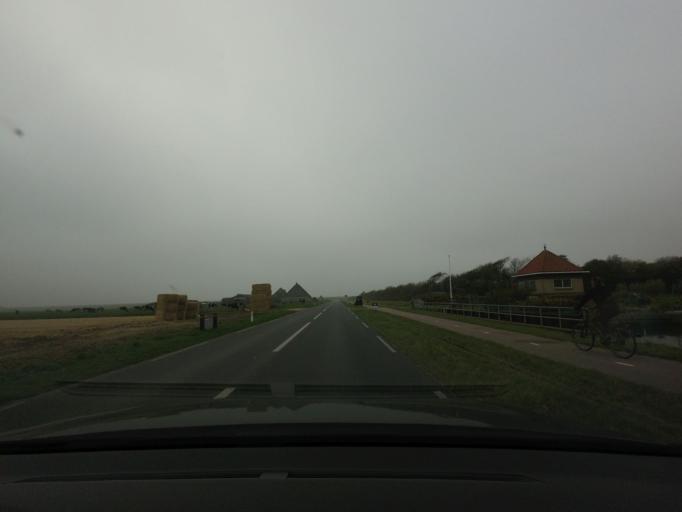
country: NL
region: North Holland
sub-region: Gemeente Schagen
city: Harenkarspel
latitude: 52.7581
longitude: 4.6675
